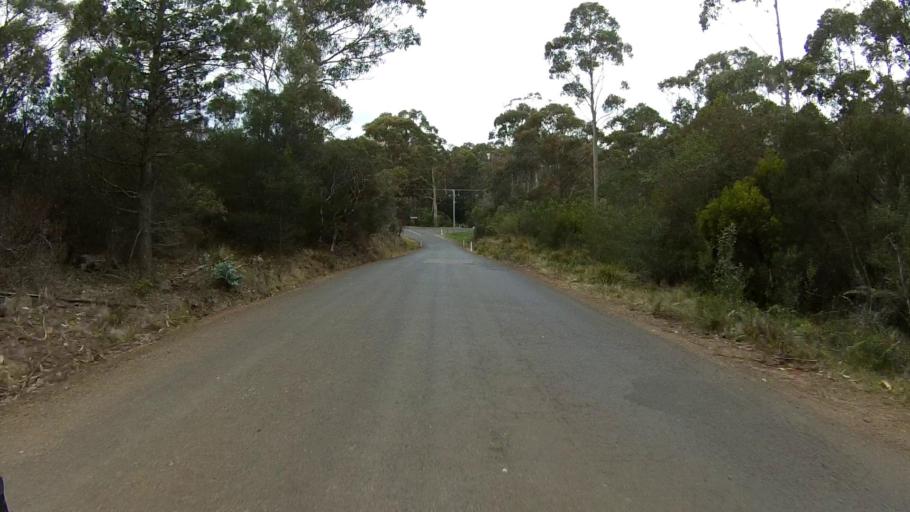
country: AU
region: Tasmania
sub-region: Sorell
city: Sorell
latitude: -42.5683
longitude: 147.8745
